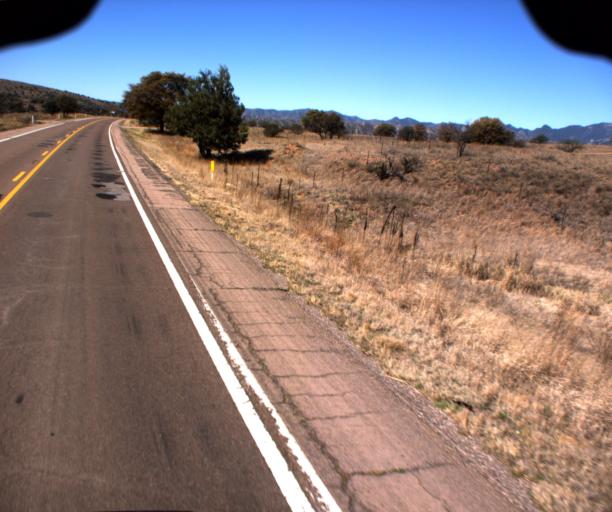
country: US
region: Arizona
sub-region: Pima County
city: Corona de Tucson
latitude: 31.6663
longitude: -110.6784
